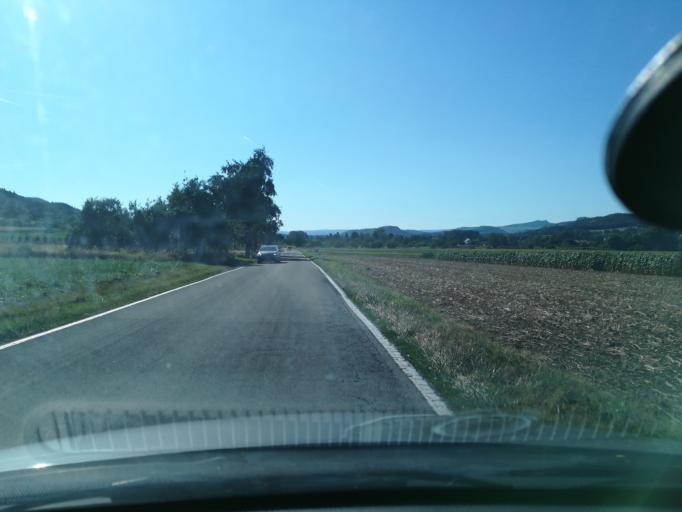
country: DE
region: Baden-Wuerttemberg
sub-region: Freiburg Region
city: Moos
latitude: 47.7121
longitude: 8.9056
